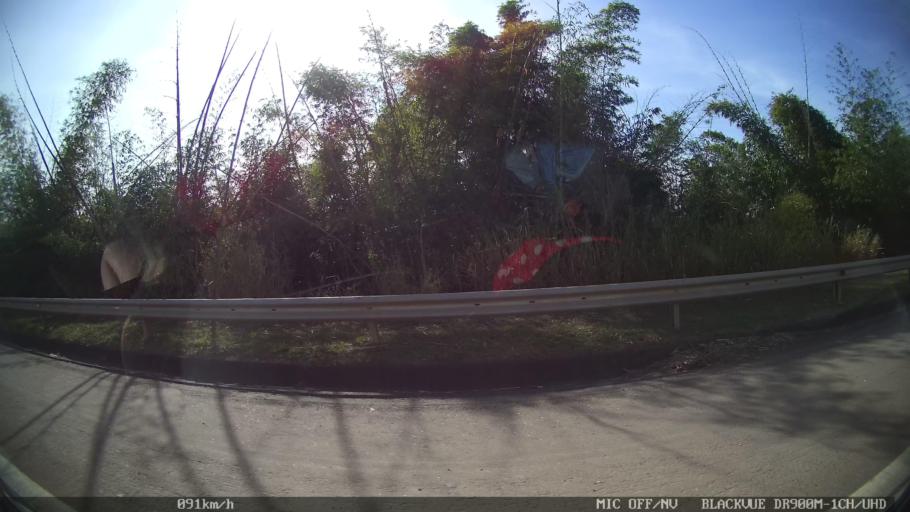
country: BR
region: Sao Paulo
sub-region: Rio Das Pedras
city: Rio das Pedras
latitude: -22.7884
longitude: -47.5839
